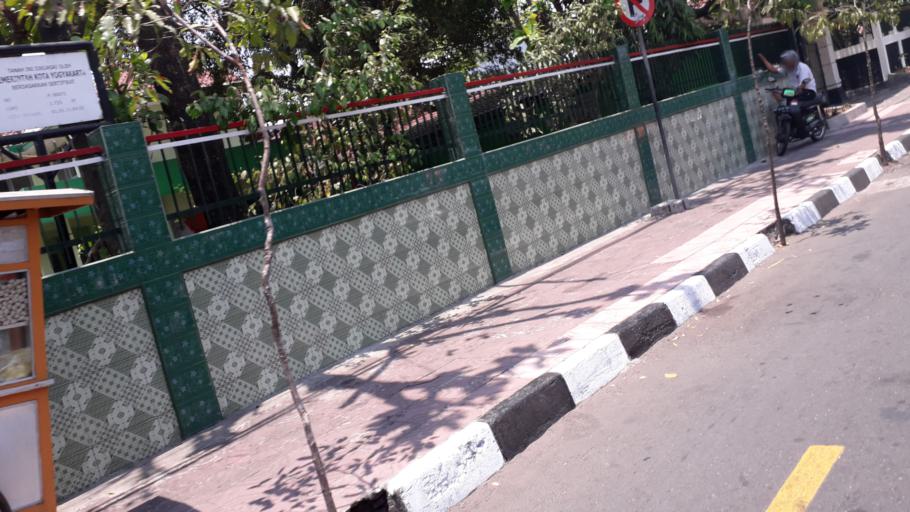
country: ID
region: Daerah Istimewa Yogyakarta
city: Yogyakarta
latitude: -7.7766
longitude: 110.3679
